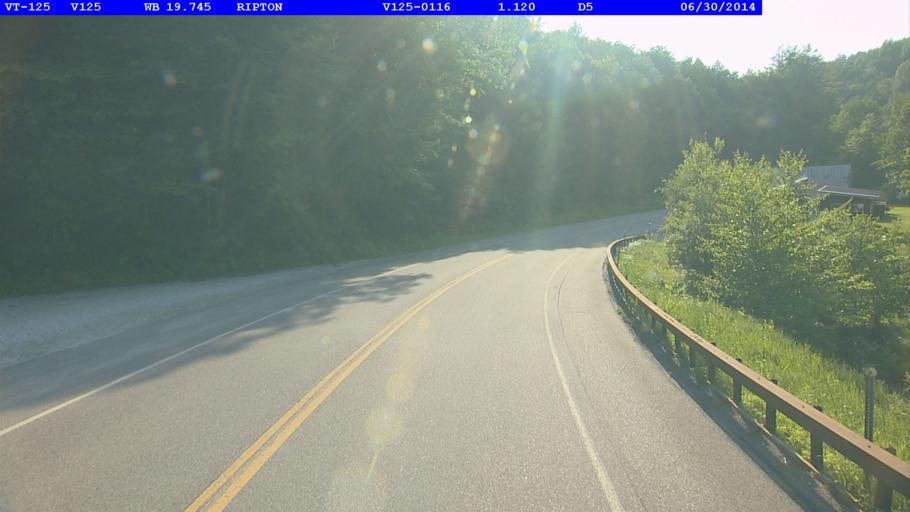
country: US
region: Vermont
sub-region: Addison County
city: Middlebury (village)
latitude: 43.9739
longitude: -73.0399
